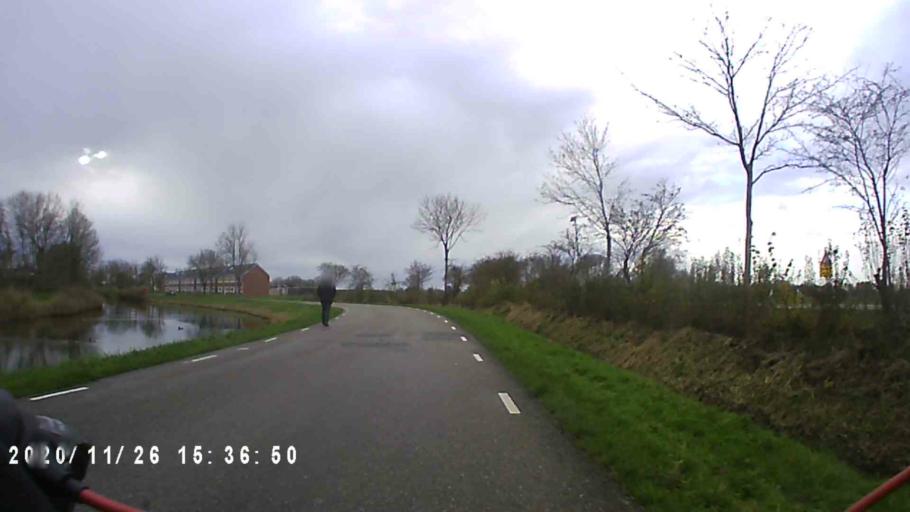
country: NL
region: Groningen
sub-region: Gemeente Slochteren
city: Slochteren
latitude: 53.3028
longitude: 6.7333
